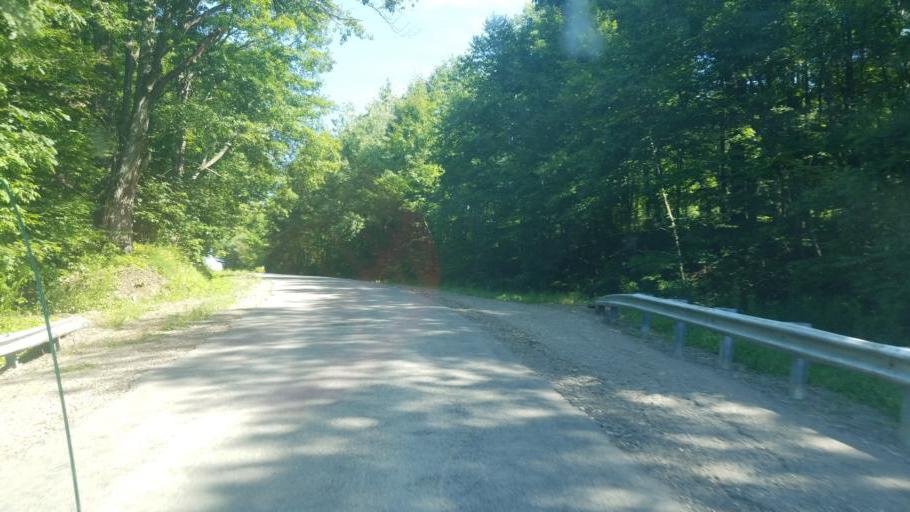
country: US
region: New York
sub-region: Allegany County
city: Bolivar
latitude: 42.0665
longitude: -78.0583
